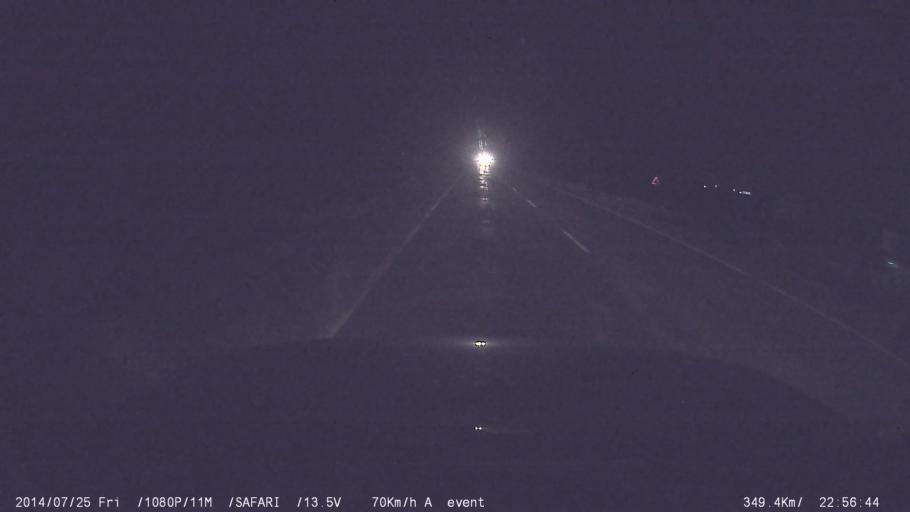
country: IN
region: Tamil Nadu
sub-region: Coimbatore
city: Singanallur
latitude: 10.9793
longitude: 77.0455
